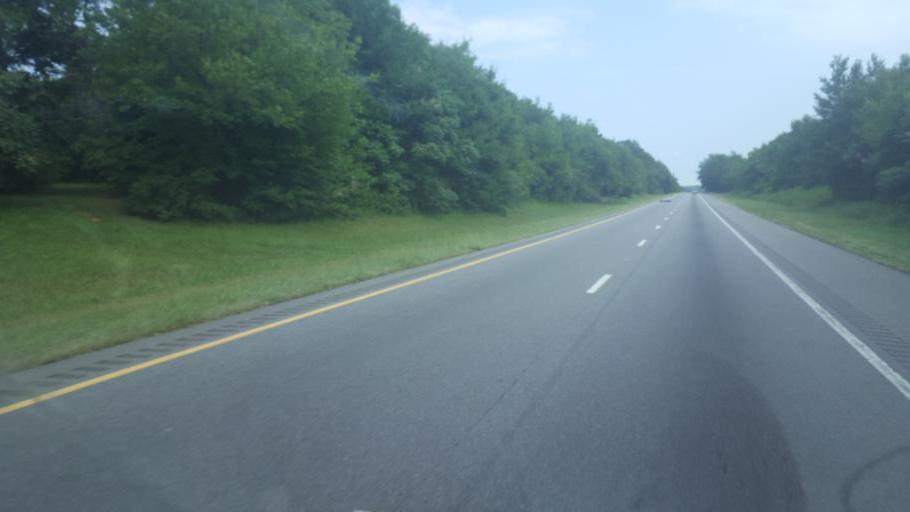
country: US
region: North Carolina
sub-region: Yadkin County
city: Jonesville
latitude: 36.0763
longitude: -80.8203
